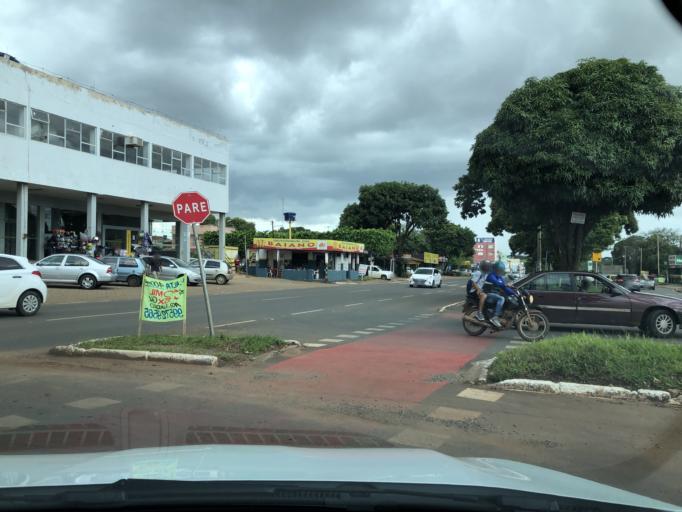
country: BR
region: Goias
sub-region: Luziania
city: Luziania
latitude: -16.0312
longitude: -48.0586
